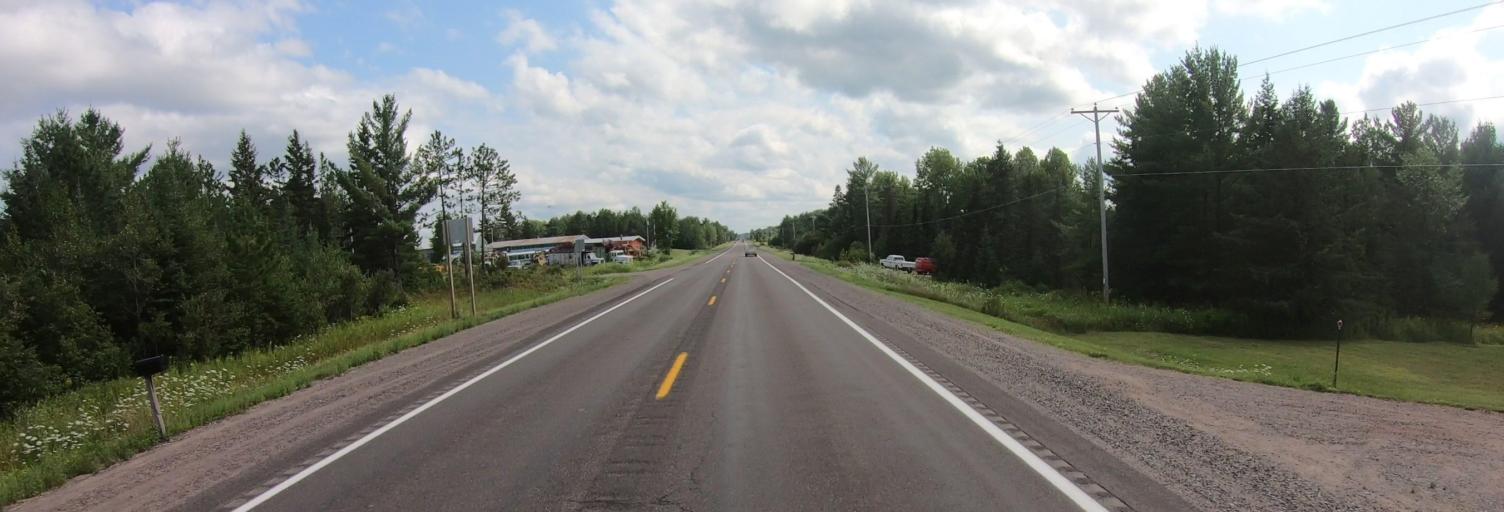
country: US
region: Michigan
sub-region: Ontonagon County
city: Ontonagon
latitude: 46.5503
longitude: -89.1787
